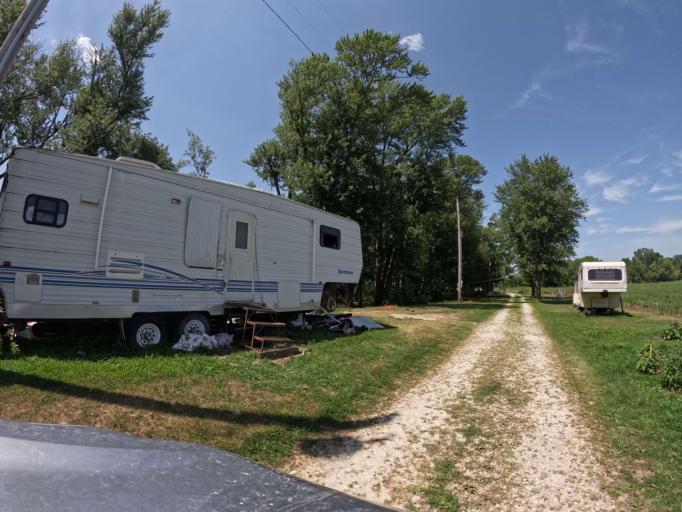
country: US
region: Iowa
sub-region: Henry County
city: Mount Pleasant
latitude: 40.8994
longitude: -91.5581
